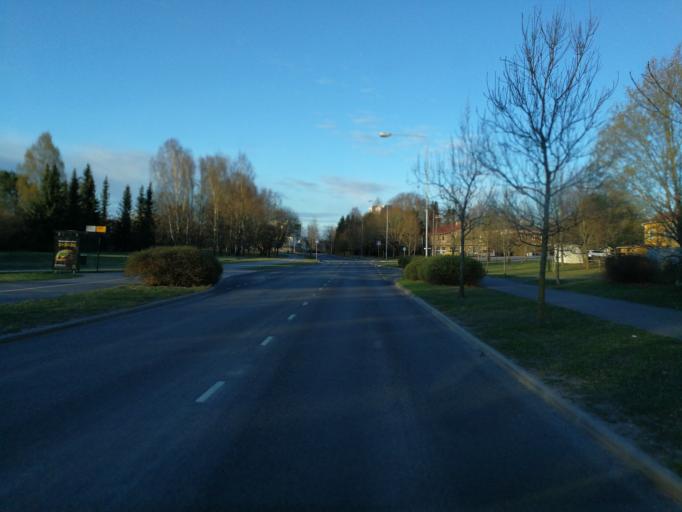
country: FI
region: Varsinais-Suomi
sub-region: Turku
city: Turku
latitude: 60.4329
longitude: 22.2409
